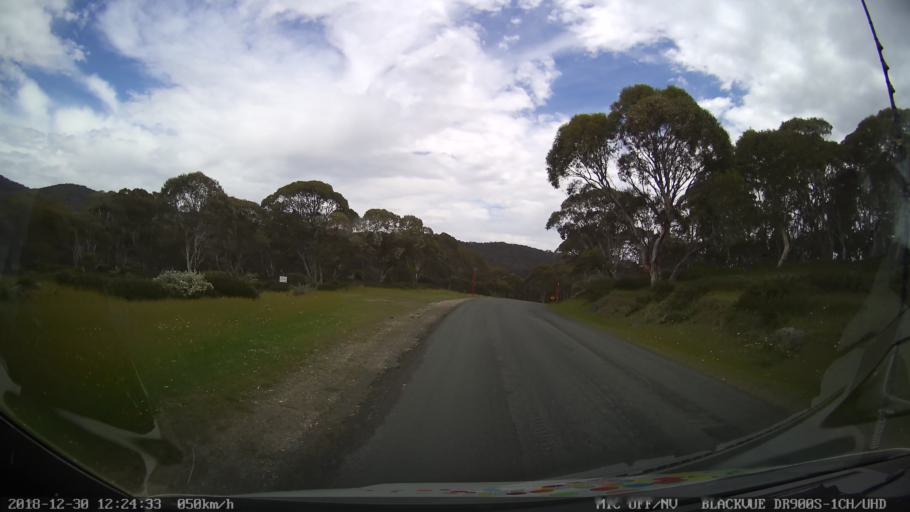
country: AU
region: New South Wales
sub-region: Snowy River
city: Jindabyne
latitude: -36.3557
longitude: 148.4913
